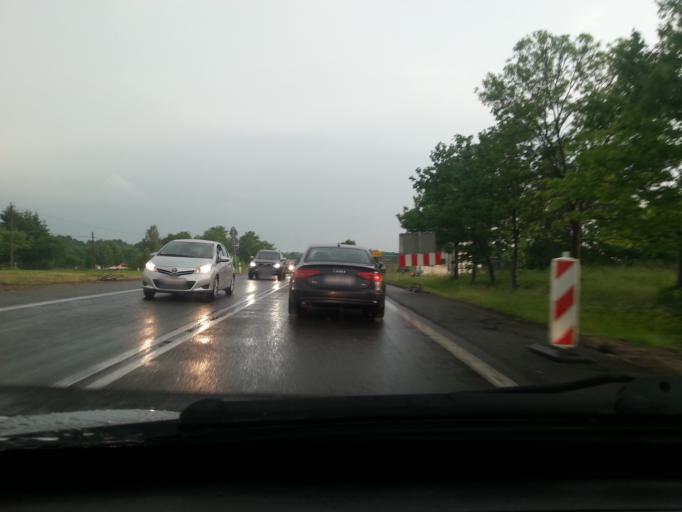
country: PL
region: Lodz Voivodeship
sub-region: Powiat zgierski
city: Strykow
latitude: 51.8756
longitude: 19.5769
